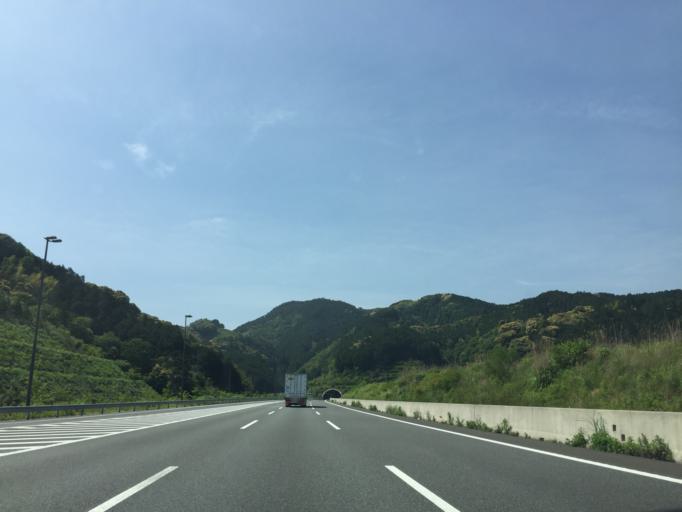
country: JP
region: Shizuoka
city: Shizuoka-shi
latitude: 34.9682
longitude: 138.2920
